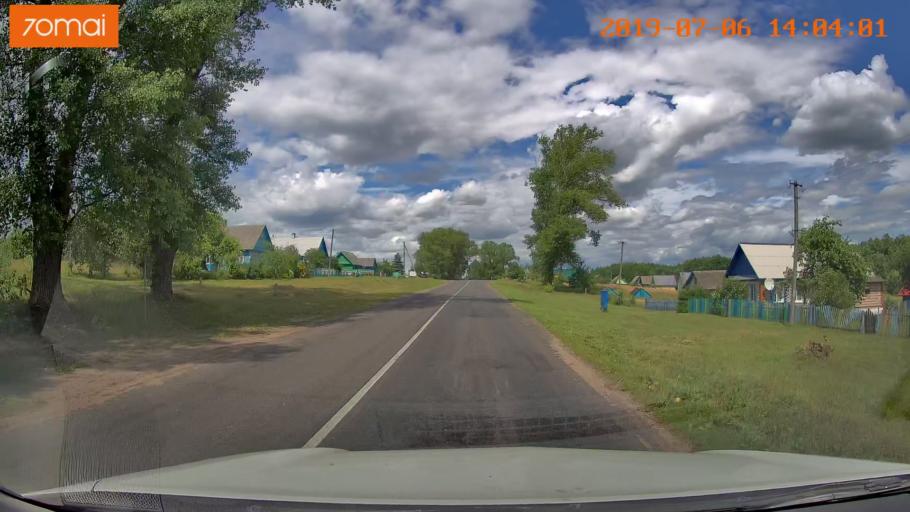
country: BY
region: Minsk
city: Ivyanyets
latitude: 53.8353
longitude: 26.8003
